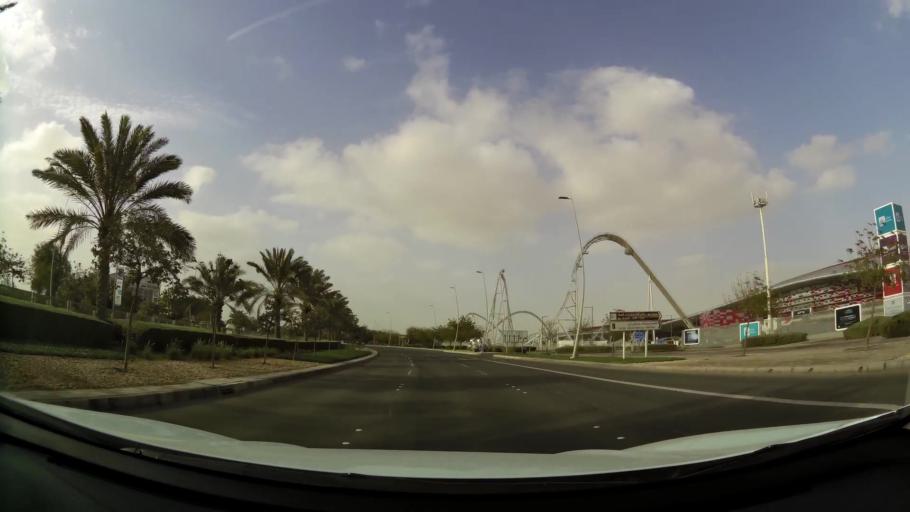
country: AE
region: Abu Dhabi
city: Abu Dhabi
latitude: 24.4816
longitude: 54.6039
